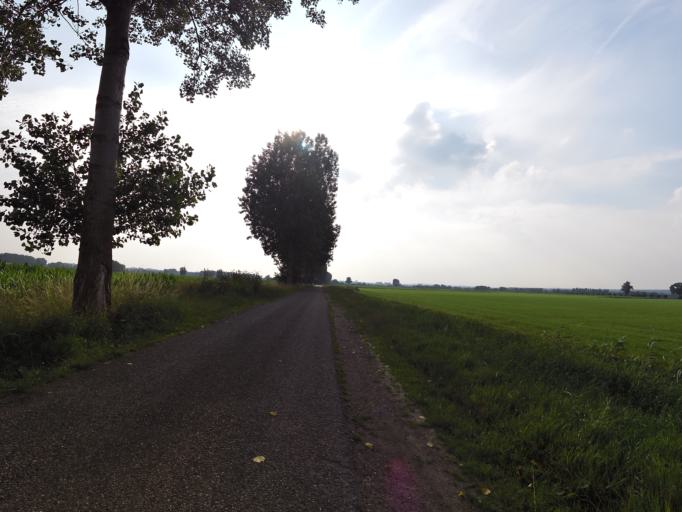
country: NL
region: Gelderland
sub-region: Gemeente Rheden
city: Rheden
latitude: 51.9783
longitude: 6.0213
